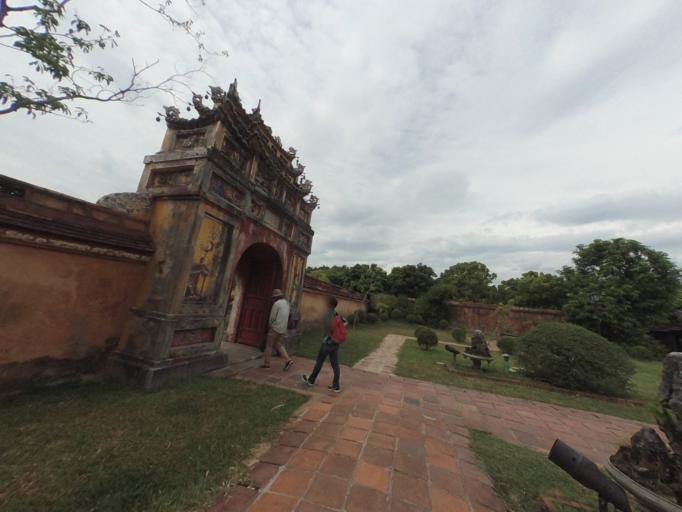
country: VN
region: Thua Thien-Hue
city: Hue
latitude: 16.4672
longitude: 107.5764
